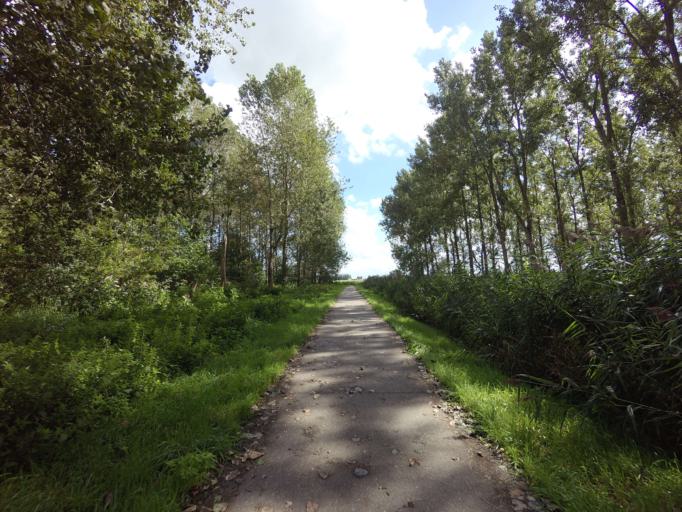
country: NL
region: North Holland
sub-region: Gemeente Purmerend
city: Purmerend
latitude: 52.4717
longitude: 4.9736
